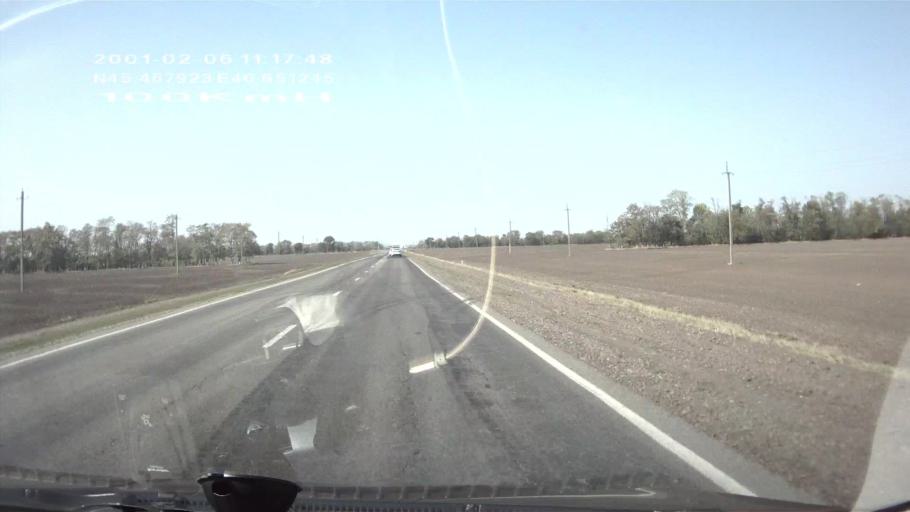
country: RU
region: Krasnodarskiy
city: Kavkazskaya
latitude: 45.4682
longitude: 40.6477
